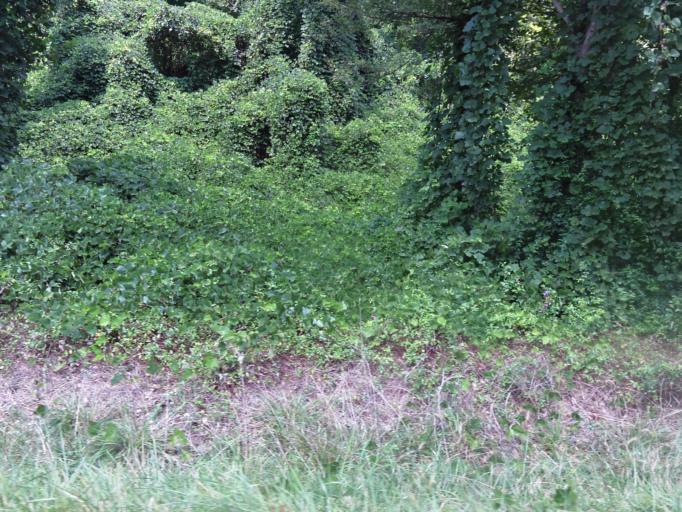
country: US
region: Kentucky
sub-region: Harlan County
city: Harlan
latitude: 36.8714
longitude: -83.3200
